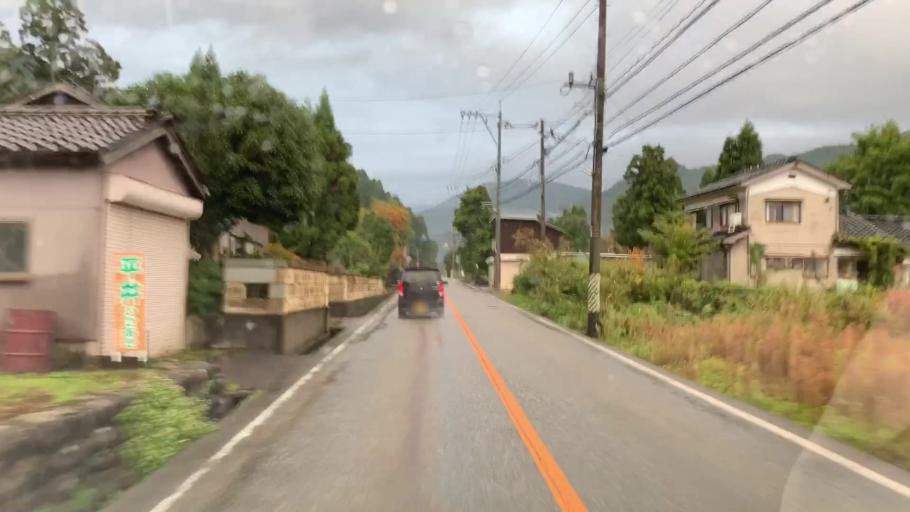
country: JP
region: Toyama
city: Kamiichi
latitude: 36.5838
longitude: 137.3349
